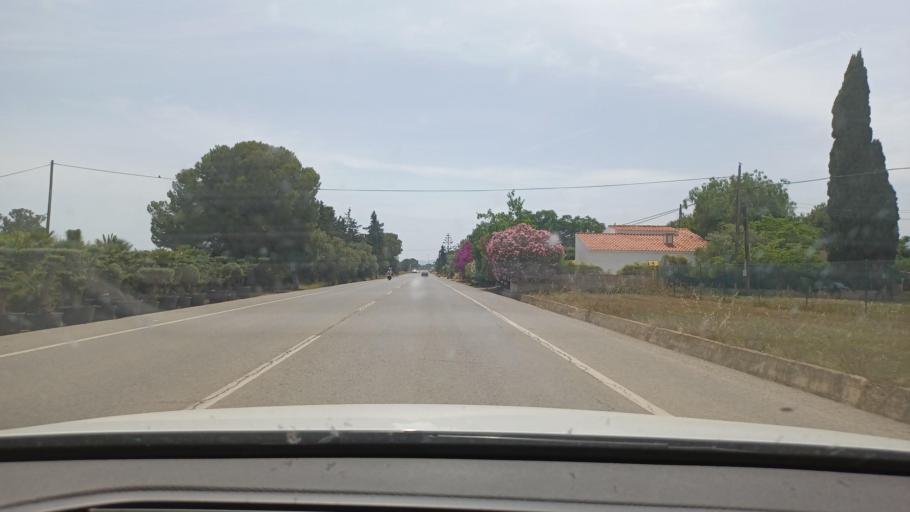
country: ES
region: Catalonia
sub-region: Provincia de Tarragona
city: Cambrils
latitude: 41.0545
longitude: 1.0063
